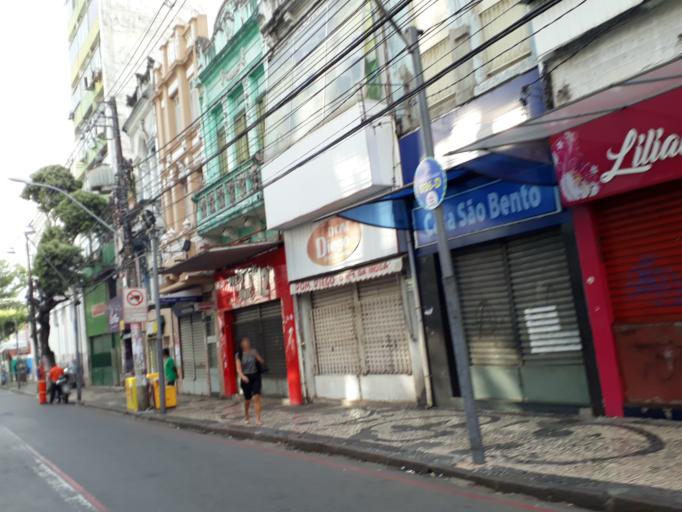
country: BR
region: Bahia
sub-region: Salvador
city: Salvador
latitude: -12.9836
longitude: -38.5163
